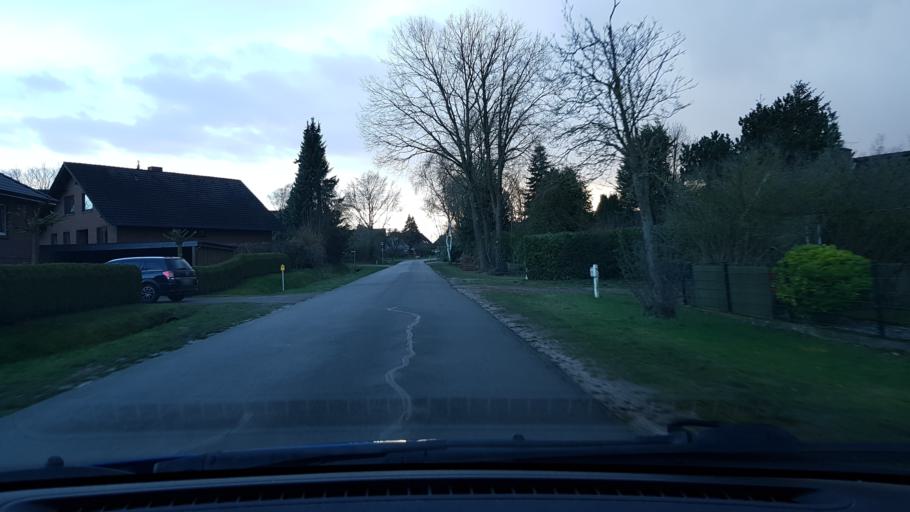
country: DE
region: Lower Saxony
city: Rullstorf
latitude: 53.2884
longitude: 10.5381
